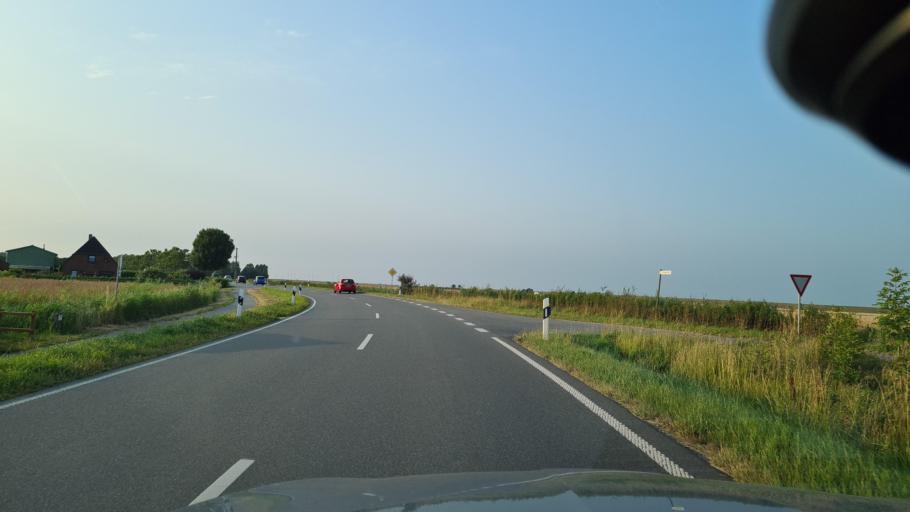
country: DE
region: Schleswig-Holstein
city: Elisabeth-Sophien-Koog
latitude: 54.5001
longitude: 8.9398
